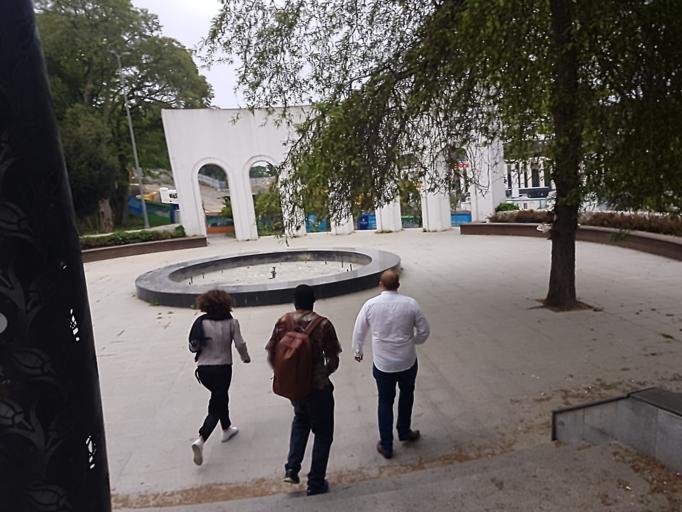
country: TR
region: Istanbul
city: Sisli
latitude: 41.0420
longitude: 28.9945
